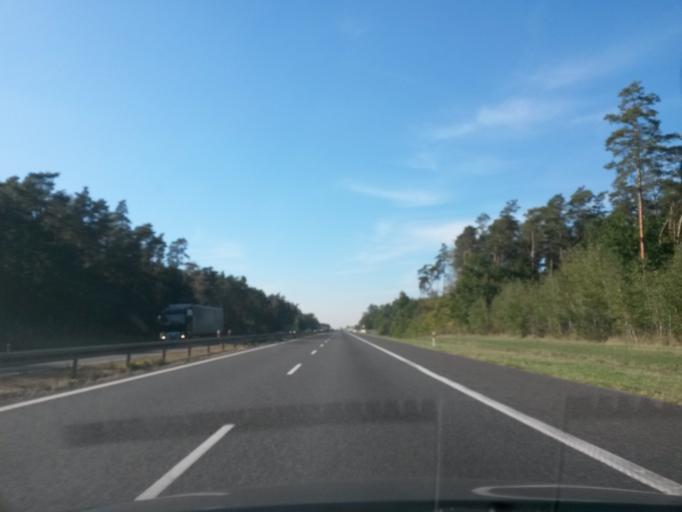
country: PL
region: Silesian Voivodeship
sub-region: Powiat gliwicki
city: Toszek
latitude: 50.3691
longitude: 18.4970
